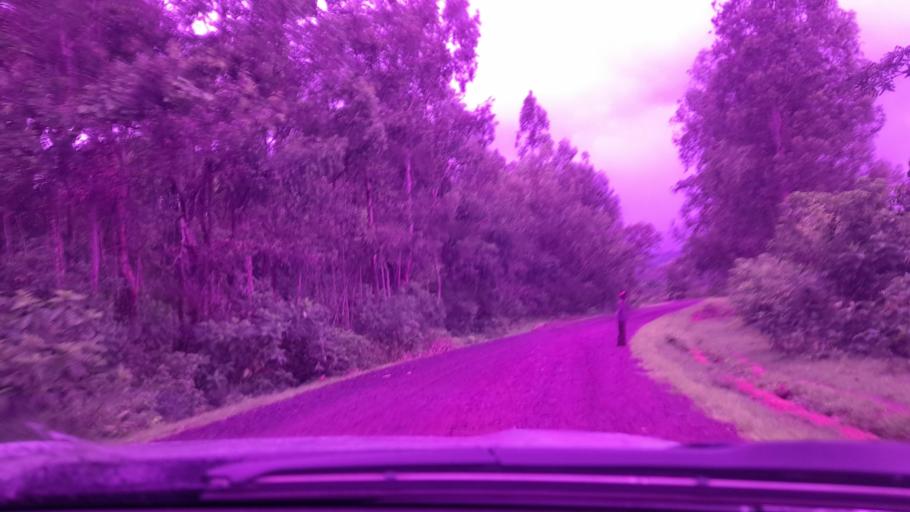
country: ET
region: Oromiya
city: Metu
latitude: 8.4350
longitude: 35.6157
